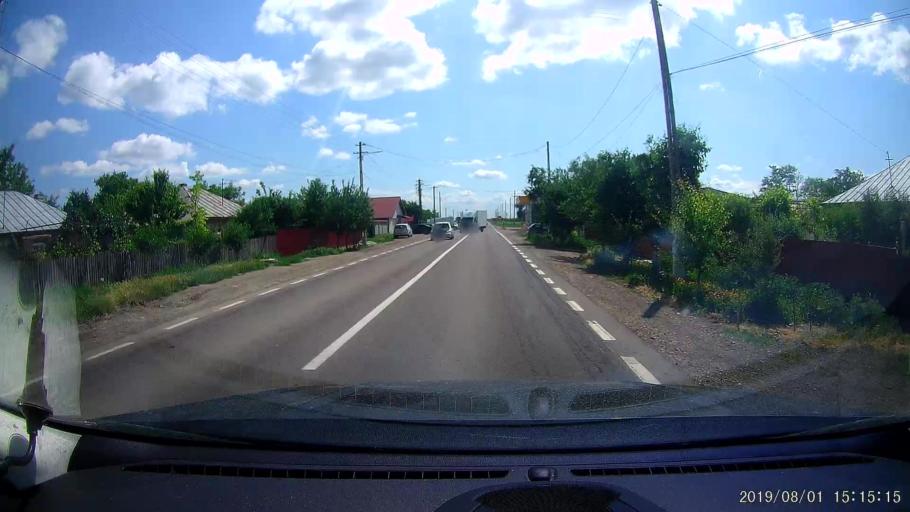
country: RO
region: Braila
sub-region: Comuna Chiscani
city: Lacu Sarat
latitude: 45.1662
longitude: 27.8700
